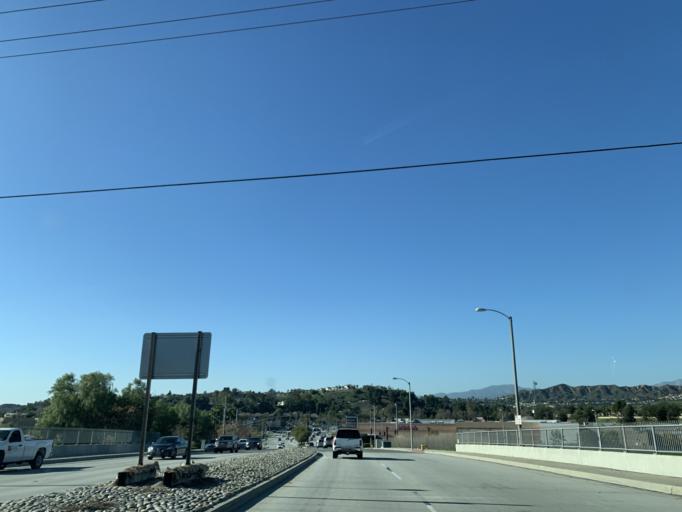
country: US
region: California
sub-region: Los Angeles County
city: Diamond Bar
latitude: 34.0249
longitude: -117.8319
